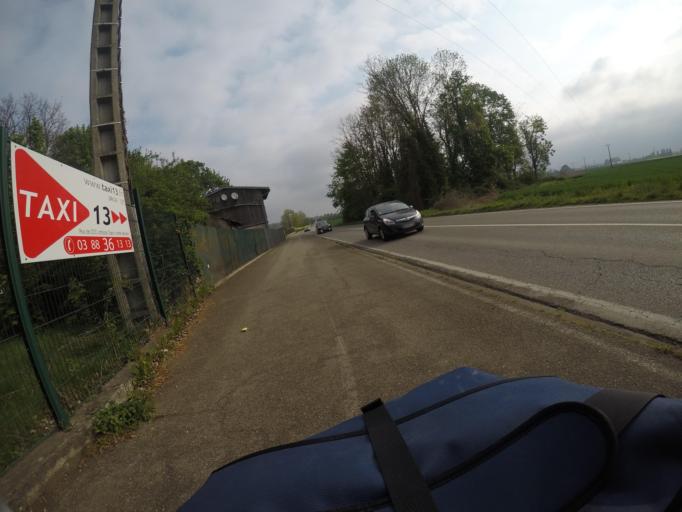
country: FR
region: Alsace
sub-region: Departement du Bas-Rhin
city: Wolfisheim
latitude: 48.5982
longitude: 7.6763
